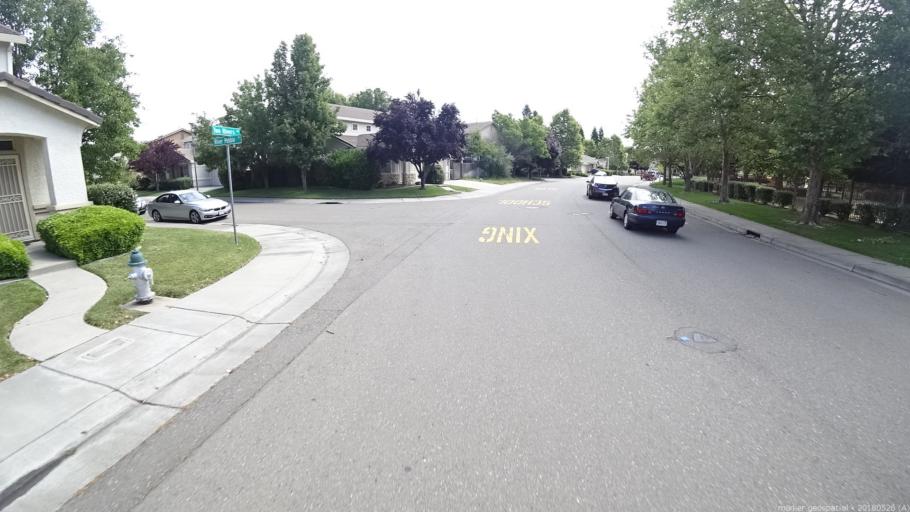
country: US
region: California
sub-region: Yolo County
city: West Sacramento
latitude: 38.6117
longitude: -121.5339
